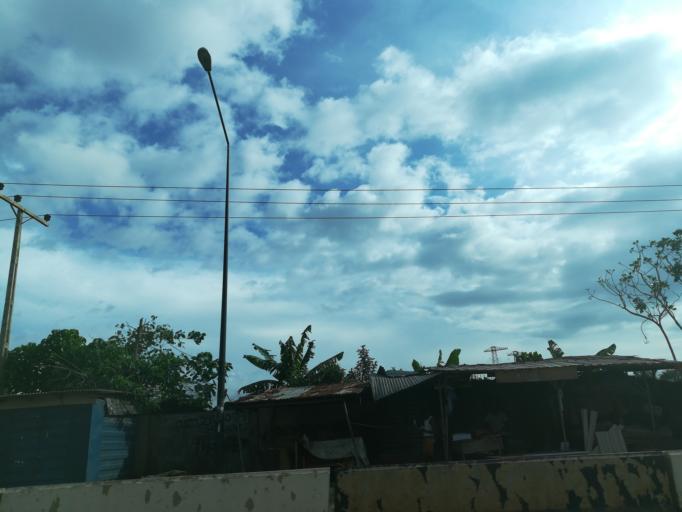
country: NG
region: Lagos
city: Ebute Ikorodu
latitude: 6.5978
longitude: 3.4988
